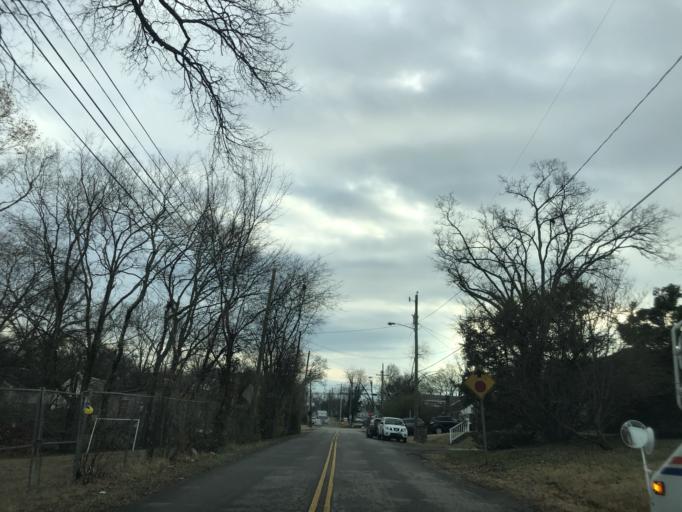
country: US
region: Tennessee
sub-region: Davidson County
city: Nashville
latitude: 36.2026
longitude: -86.7326
